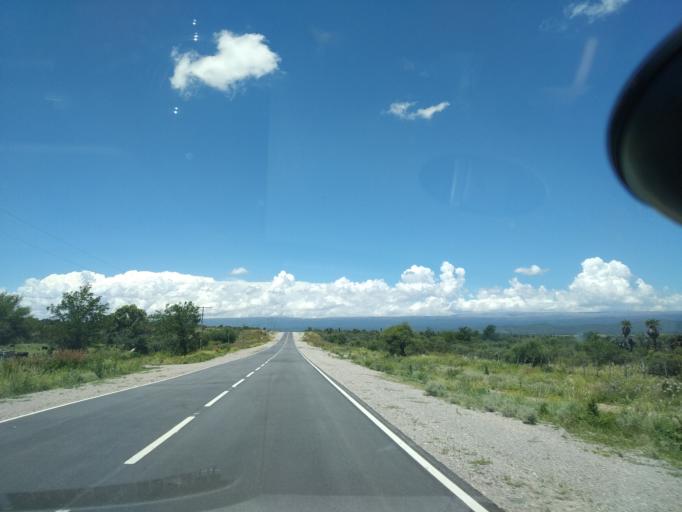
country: AR
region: Cordoba
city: Salsacate
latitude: -31.3585
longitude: -65.1687
